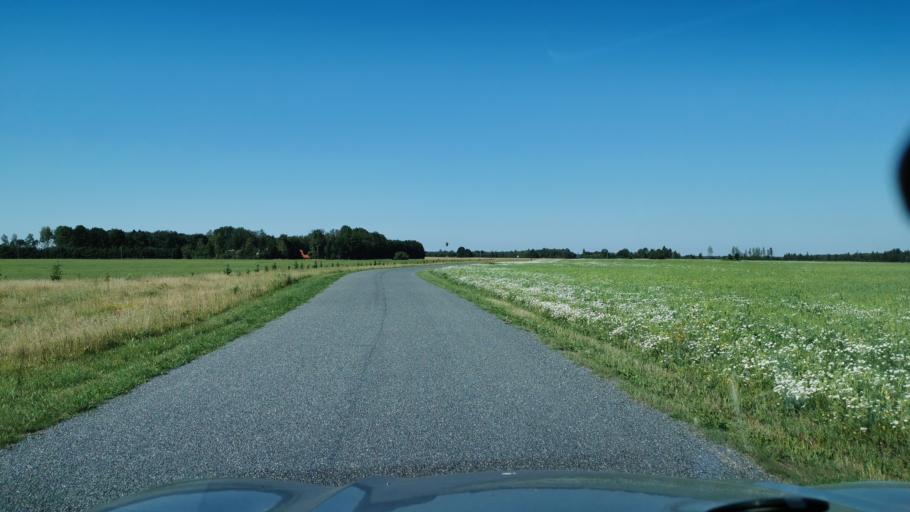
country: EE
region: Harju
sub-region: Paldiski linn
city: Paldiski
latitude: 59.2077
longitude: 24.0050
